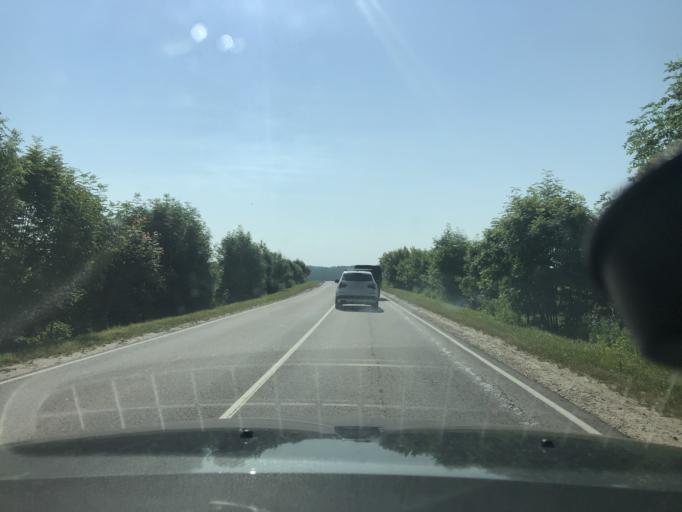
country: RU
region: Tula
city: Dubna
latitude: 54.1340
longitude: 37.0257
